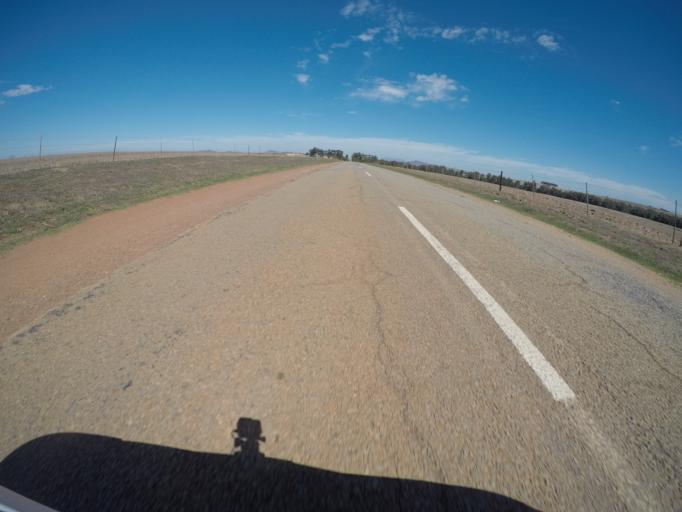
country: ZA
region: Western Cape
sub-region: City of Cape Town
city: Atlantis
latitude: -33.6061
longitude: 18.6392
